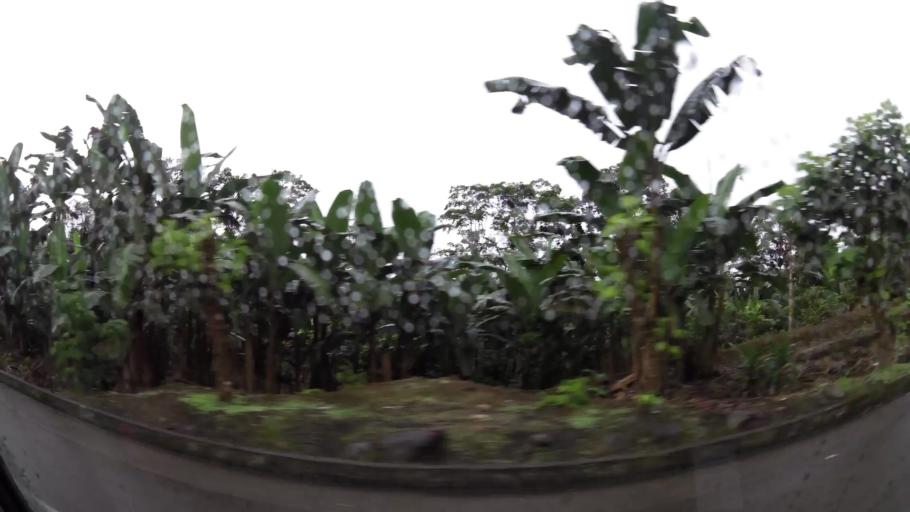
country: EC
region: Santo Domingo de los Tsachilas
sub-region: Canton Santo Domingo de los Colorados
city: Santo Domingo de los Colorados
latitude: -0.2373
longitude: -79.1368
